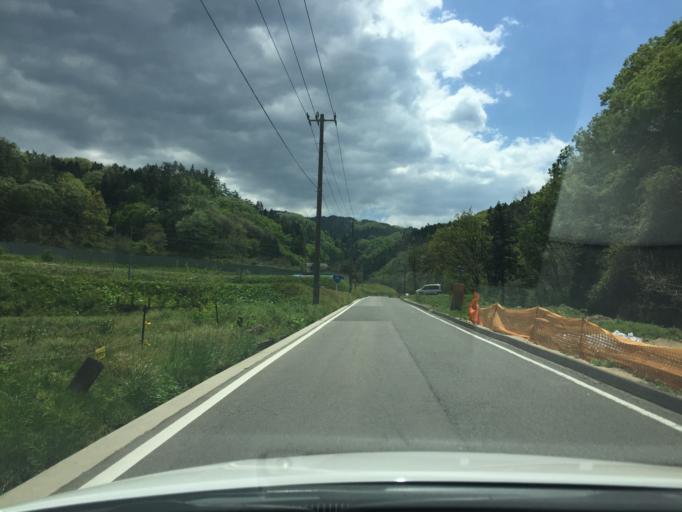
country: JP
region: Fukushima
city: Hobaramachi
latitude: 37.7338
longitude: 140.6331
